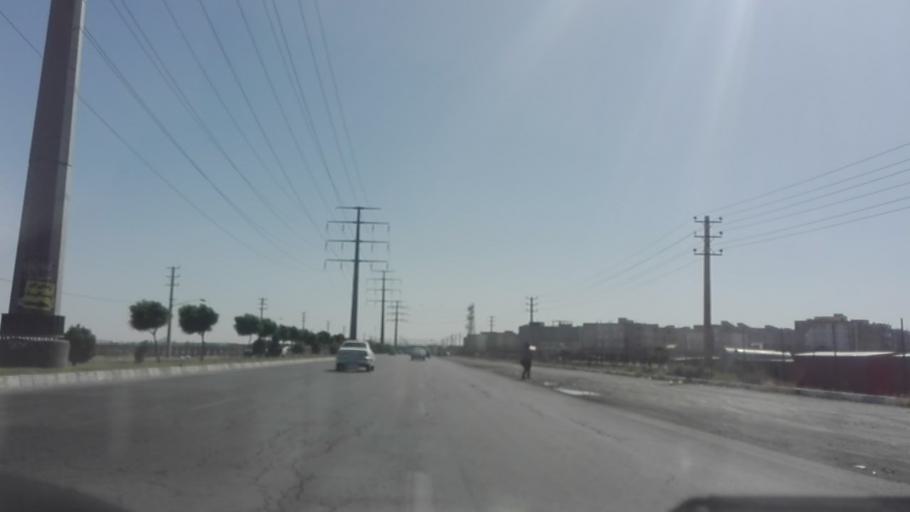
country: IR
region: Tehran
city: Shahre Jadide Andisheh
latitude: 35.6625
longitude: 51.0158
